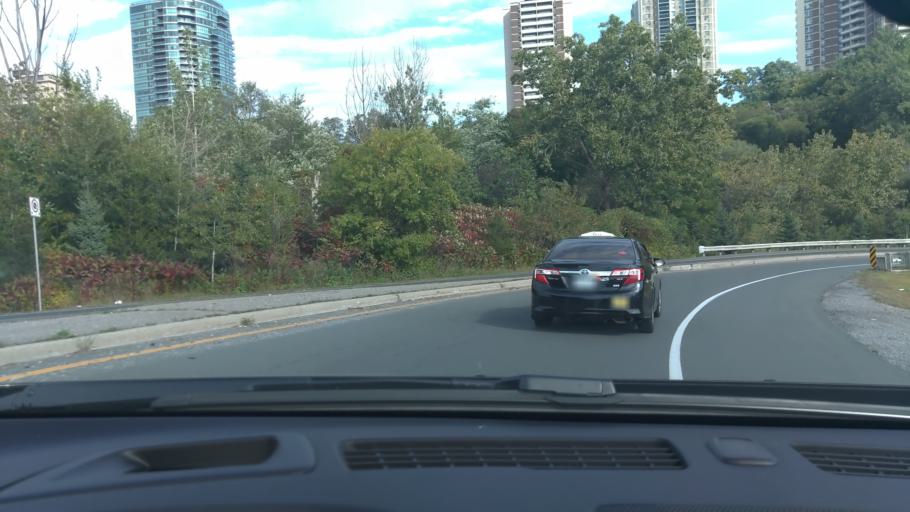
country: CA
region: Ontario
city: Toronto
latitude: 43.6837
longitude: -79.3609
